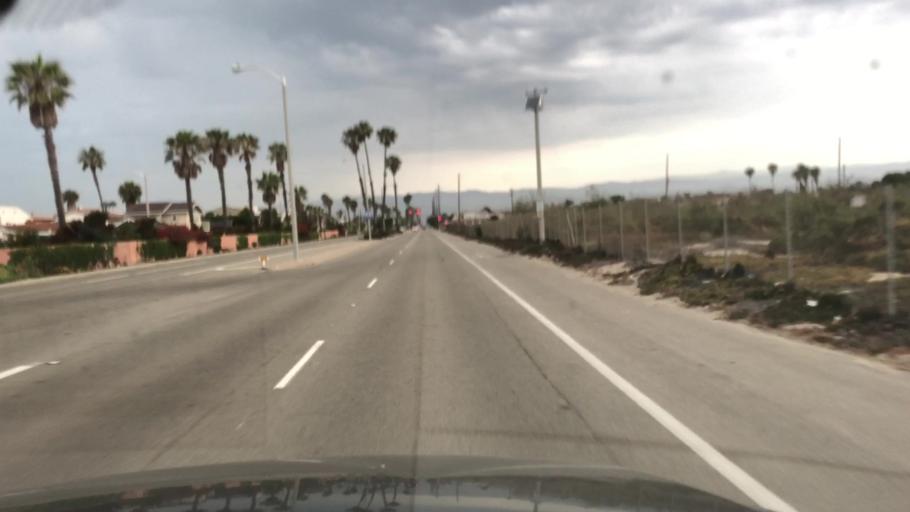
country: US
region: California
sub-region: Ventura County
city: Oxnard Shores
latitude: 34.1880
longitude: -119.2371
